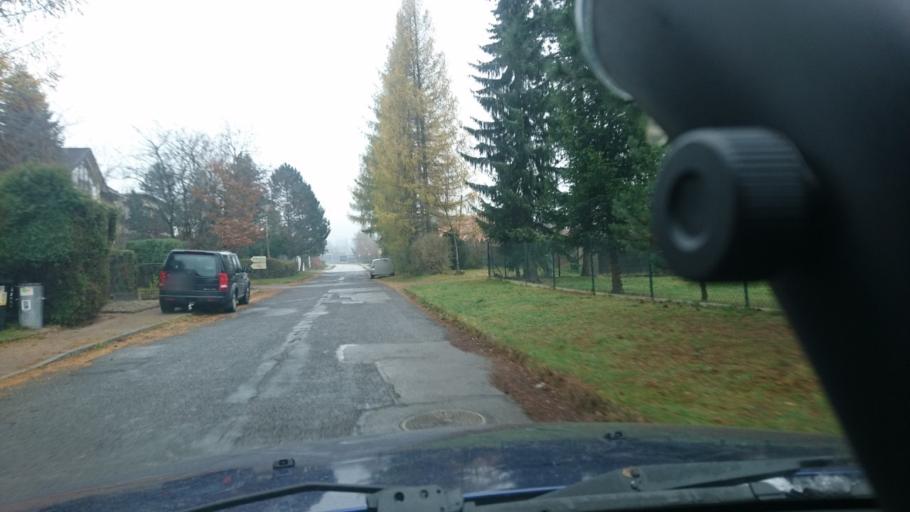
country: PL
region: Silesian Voivodeship
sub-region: Bielsko-Biala
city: Bielsko-Biala
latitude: 49.7953
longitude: 19.0714
